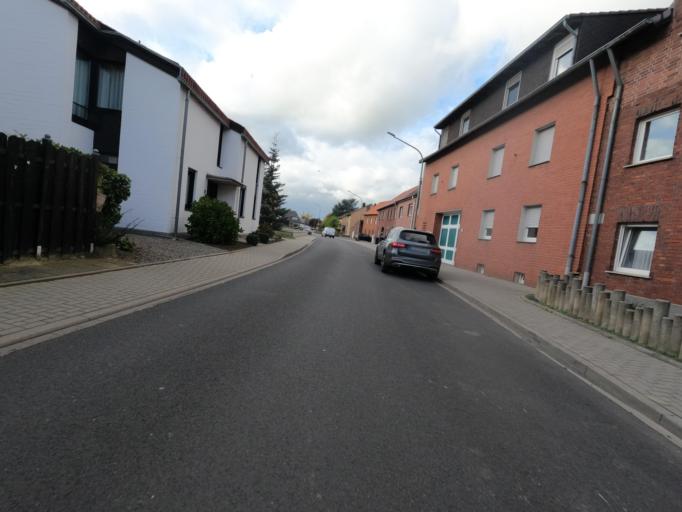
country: DE
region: North Rhine-Westphalia
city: Geilenkirchen
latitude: 50.9690
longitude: 6.1072
